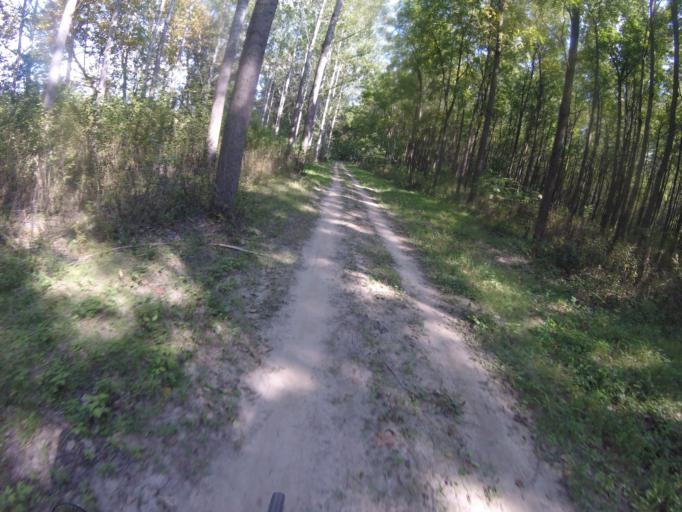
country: HU
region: Bacs-Kiskun
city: Baja
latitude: 46.1957
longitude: 18.8798
